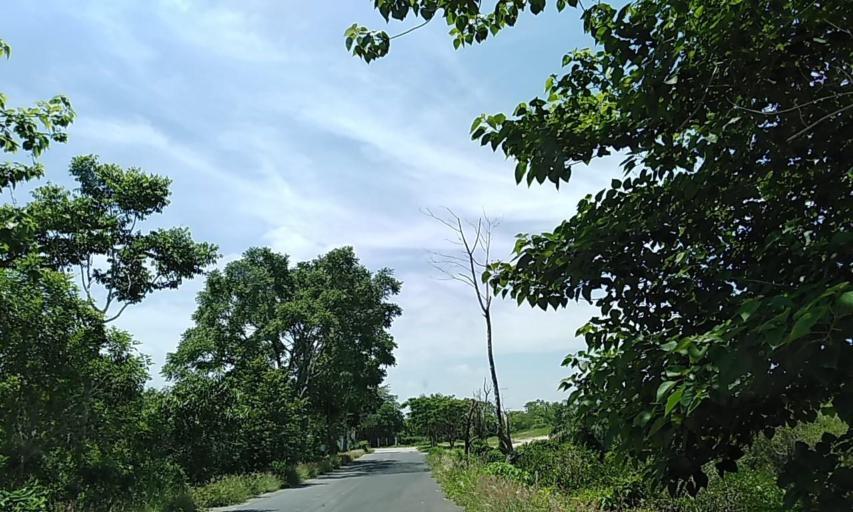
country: MX
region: Veracruz
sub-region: Emiliano Zapata
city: Dos Rios
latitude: 19.4414
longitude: -96.7582
